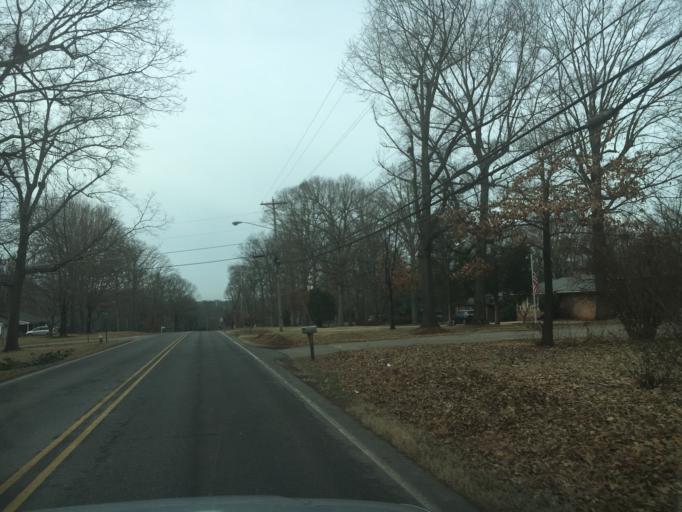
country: US
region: North Carolina
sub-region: Iredell County
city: Statesville
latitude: 35.7984
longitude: -80.8321
